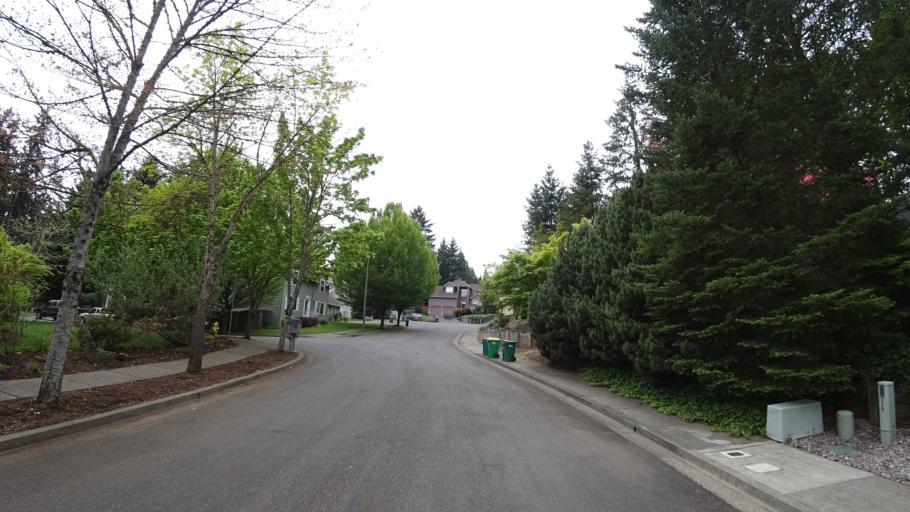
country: US
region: Oregon
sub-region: Washington County
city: Beaverton
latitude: 45.4490
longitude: -122.8367
